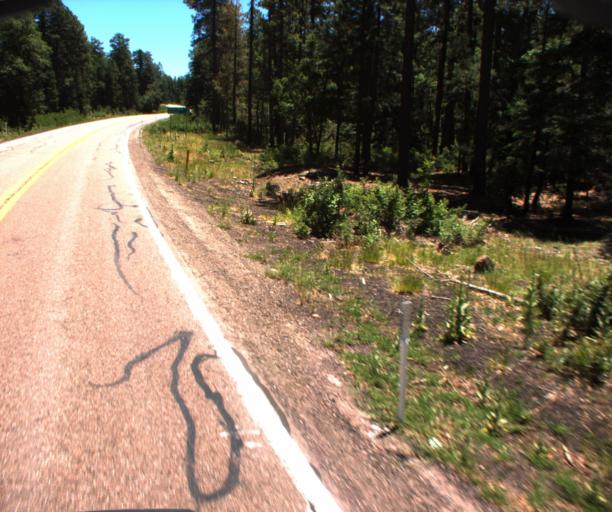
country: US
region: Arizona
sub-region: Gila County
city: Pine
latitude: 34.4569
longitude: -111.4048
